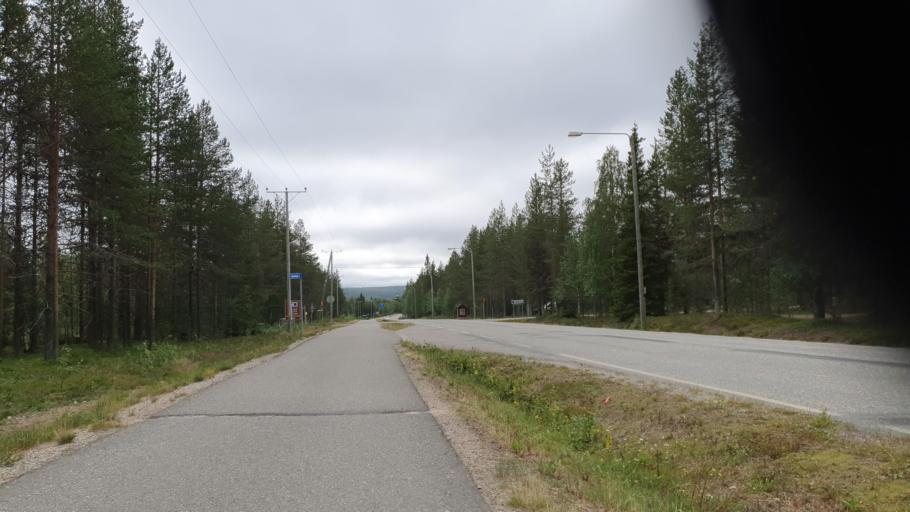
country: FI
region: Lapland
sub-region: Tunturi-Lappi
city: Kolari
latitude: 67.6214
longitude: 24.1543
